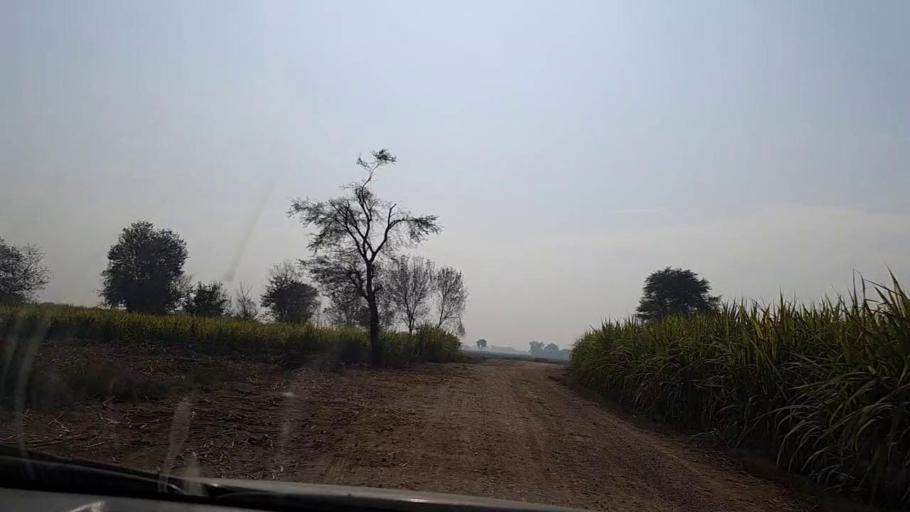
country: PK
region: Sindh
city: Daulatpur
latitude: 26.5402
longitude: 67.9878
